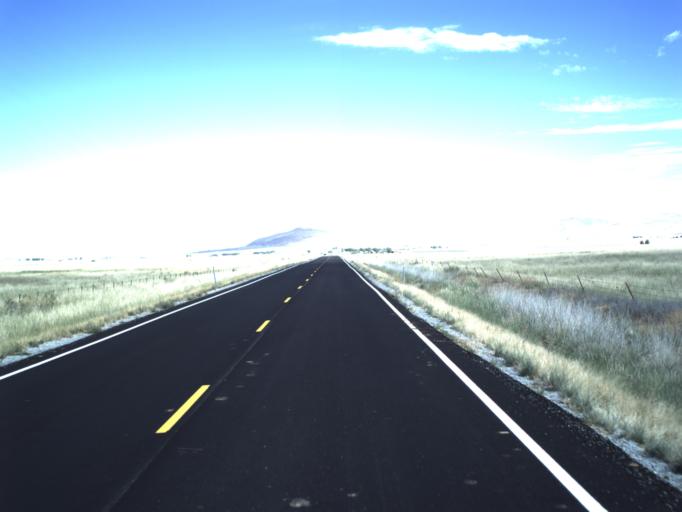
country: US
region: Utah
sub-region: Box Elder County
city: Tremonton
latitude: 41.7457
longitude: -112.4344
